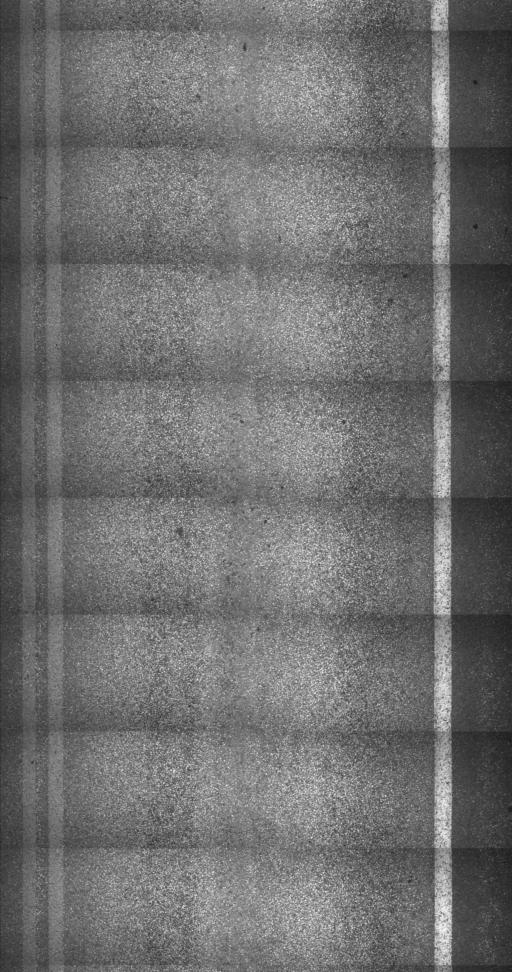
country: US
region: Vermont
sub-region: Grand Isle County
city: North Hero
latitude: 44.7146
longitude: -73.2975
